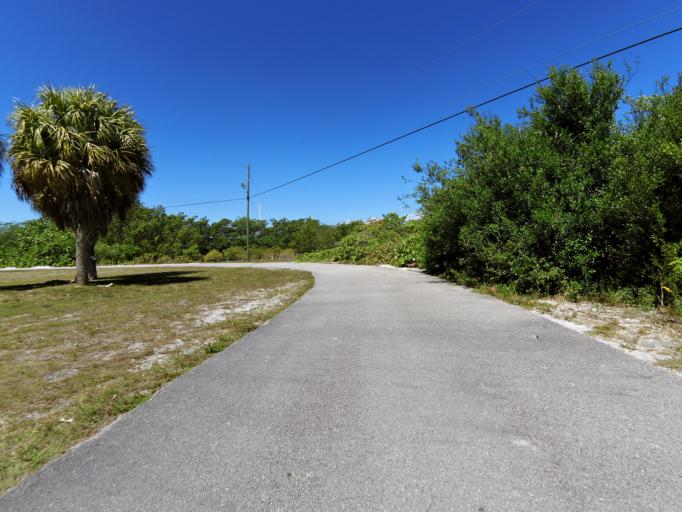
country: US
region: Florida
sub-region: Miami-Dade County
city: Key Biscayne
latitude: 25.6762
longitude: -80.1607
